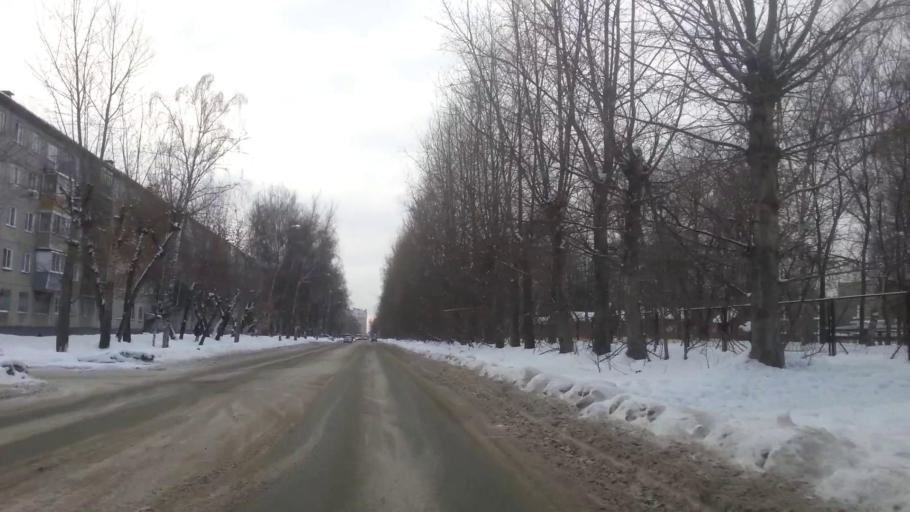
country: RU
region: Altai Krai
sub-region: Gorod Barnaulskiy
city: Barnaul
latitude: 53.3682
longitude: 83.6935
